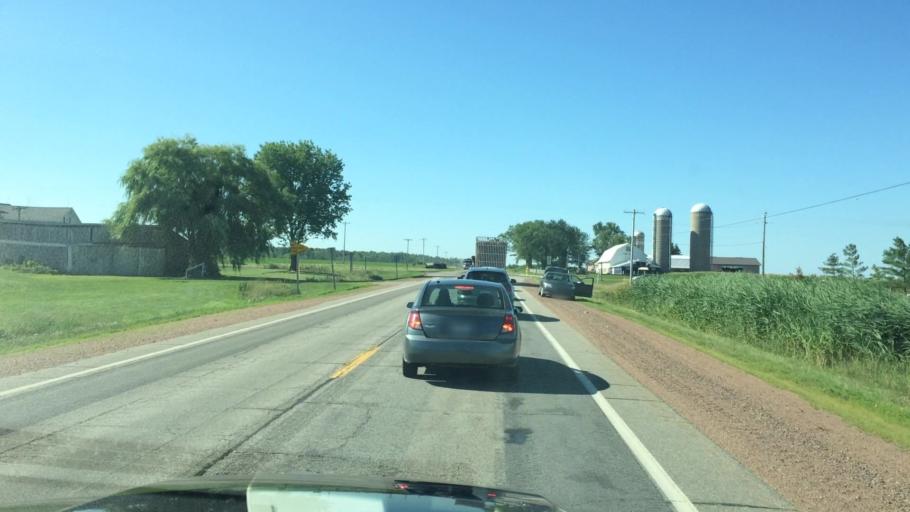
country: US
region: Wisconsin
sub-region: Marathon County
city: Stratford
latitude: 44.9034
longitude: -90.0787
